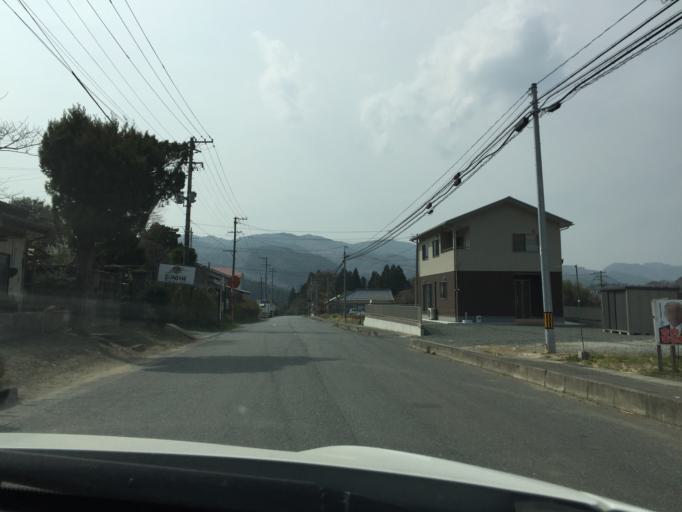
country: JP
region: Fukushima
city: Iwaki
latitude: 37.0324
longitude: 140.7186
